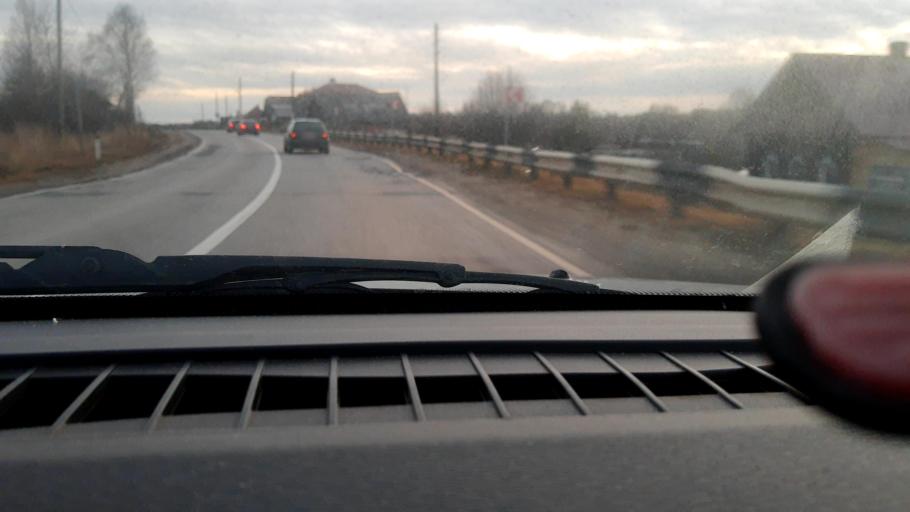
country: RU
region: Nizjnij Novgorod
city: Krasnyye Baki
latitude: 57.0680
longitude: 45.1373
